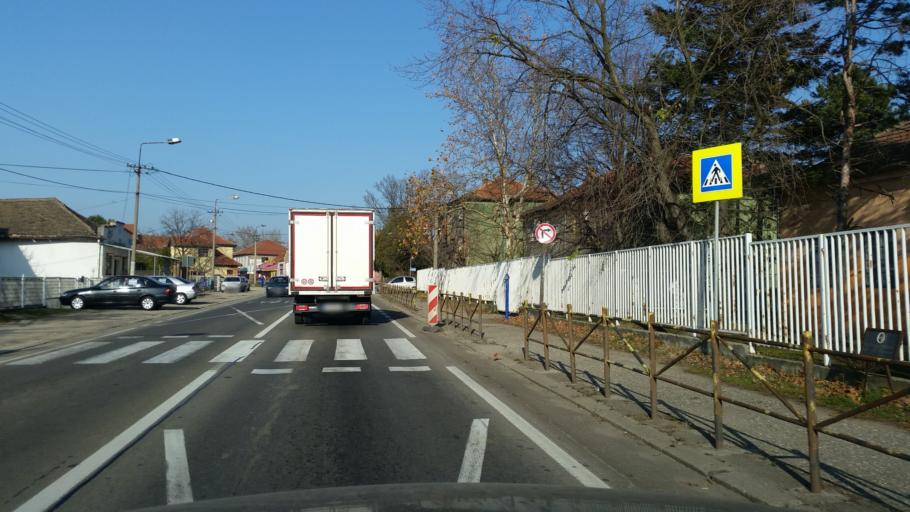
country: RS
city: Stepojevac
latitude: 44.5113
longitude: 20.2947
